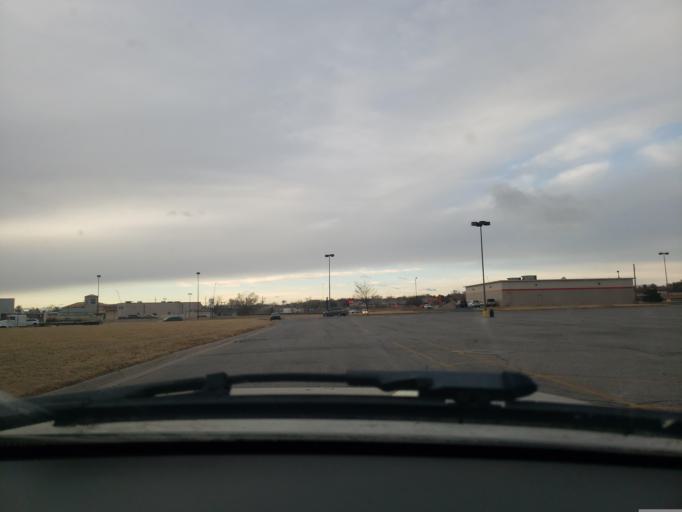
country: US
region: Kansas
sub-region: Finney County
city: Garden City
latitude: 37.9754
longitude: -100.8438
